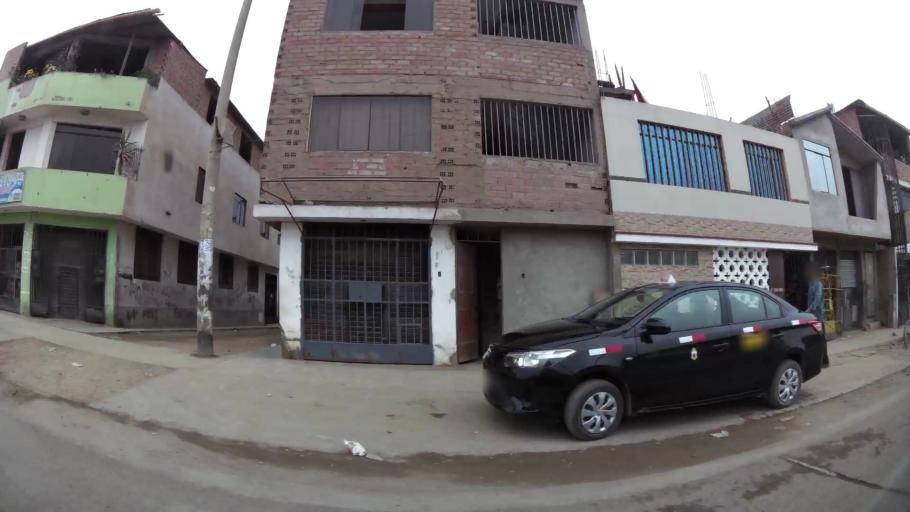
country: PE
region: Lima
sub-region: Lima
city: Surco
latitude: -12.2356
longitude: -76.9224
